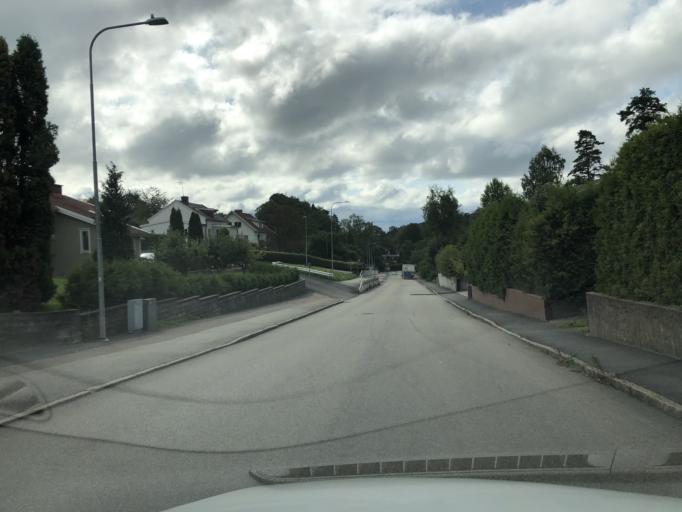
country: SE
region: Vaestra Goetaland
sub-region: Goteborg
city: Majorna
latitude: 57.7392
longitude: 11.9132
